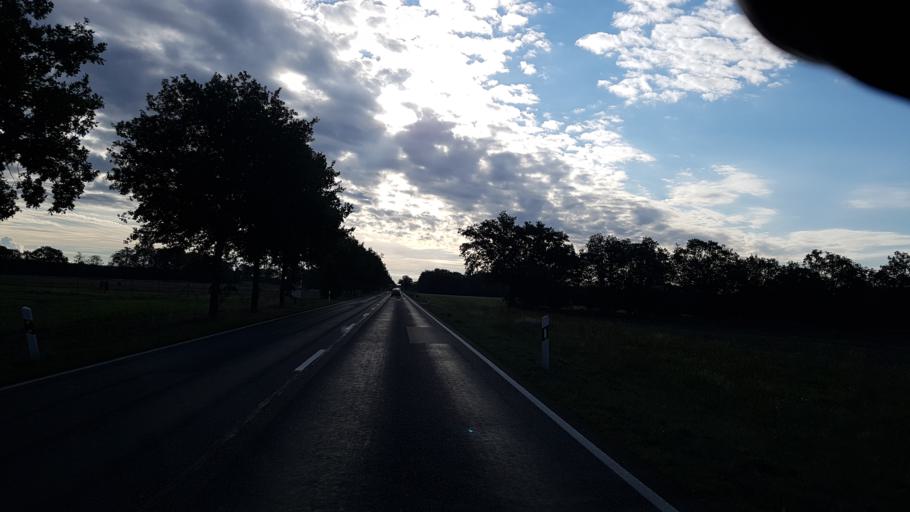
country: DE
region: Brandenburg
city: Grossraschen
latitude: 51.5772
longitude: 14.0507
